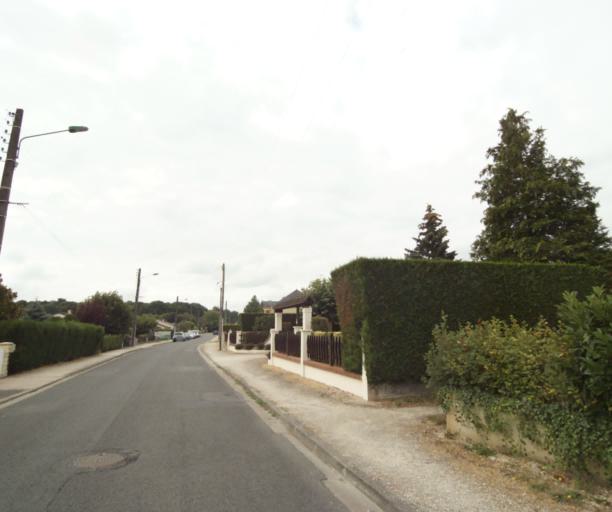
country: FR
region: Centre
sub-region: Departement du Loiret
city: Boigny-sur-Bionne
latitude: 47.9295
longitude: 2.0088
